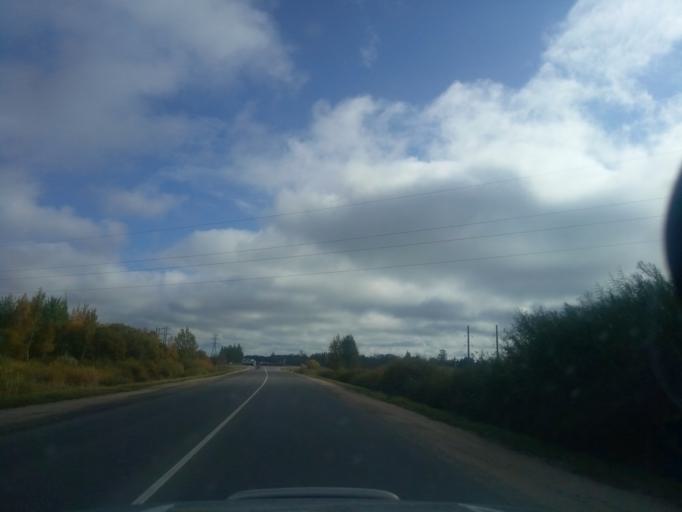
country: BY
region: Minsk
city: Zaslawye
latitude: 54.0018
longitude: 27.2721
